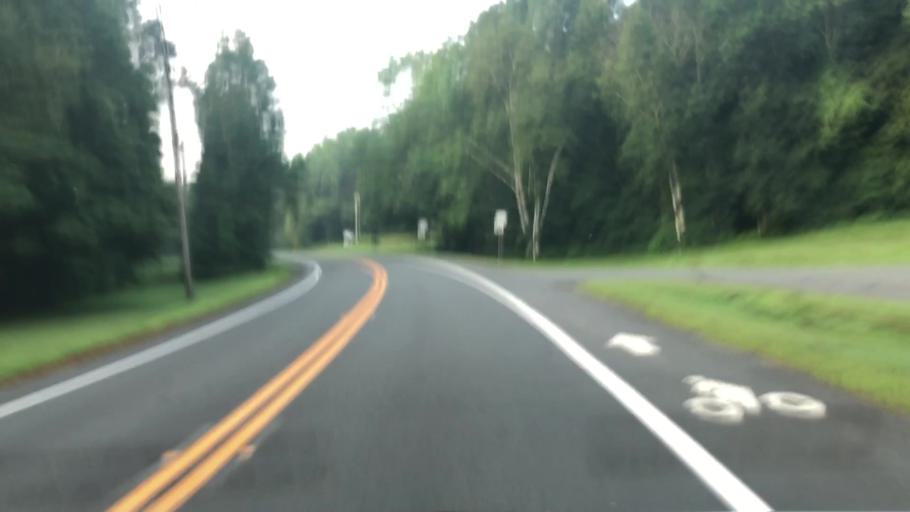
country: US
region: Massachusetts
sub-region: Franklin County
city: Buckland
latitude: 42.5646
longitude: -72.8037
